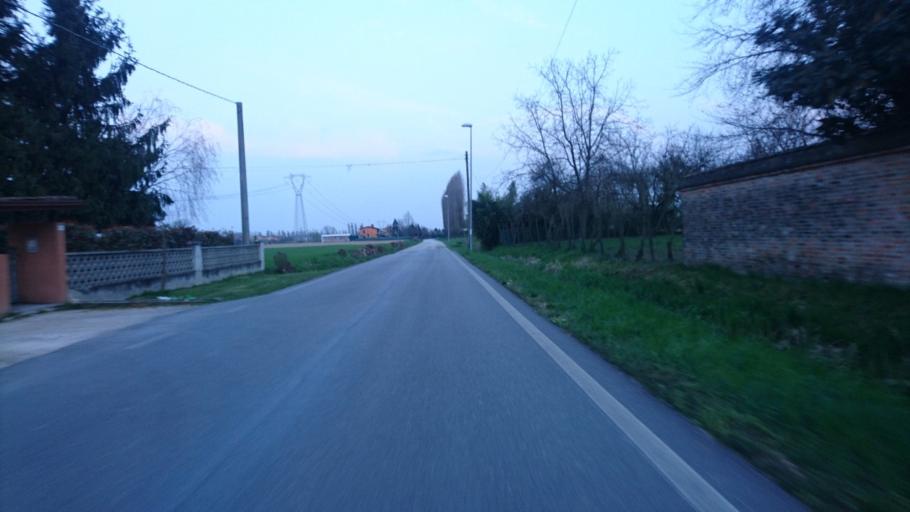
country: IT
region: Veneto
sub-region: Provincia di Padova
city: Saccolongo
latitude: 45.3909
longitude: 11.7532
